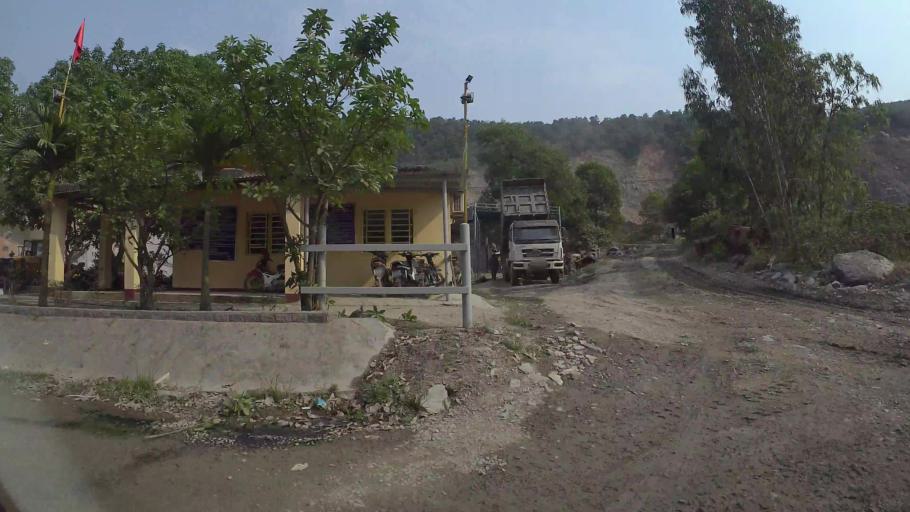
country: VN
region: Da Nang
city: Lien Chieu
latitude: 16.0397
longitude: 108.1587
